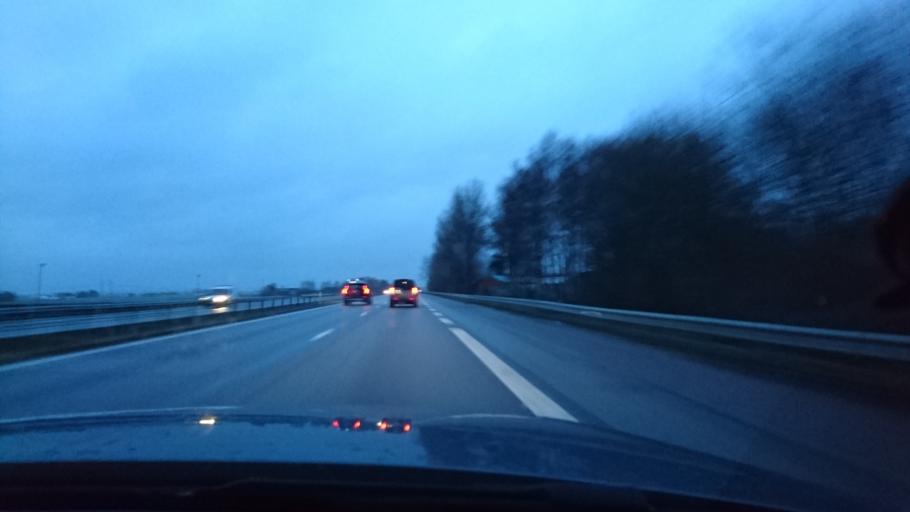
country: SE
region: Skane
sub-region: Helsingborg
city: Hyllinge
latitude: 56.1052
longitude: 12.8580
